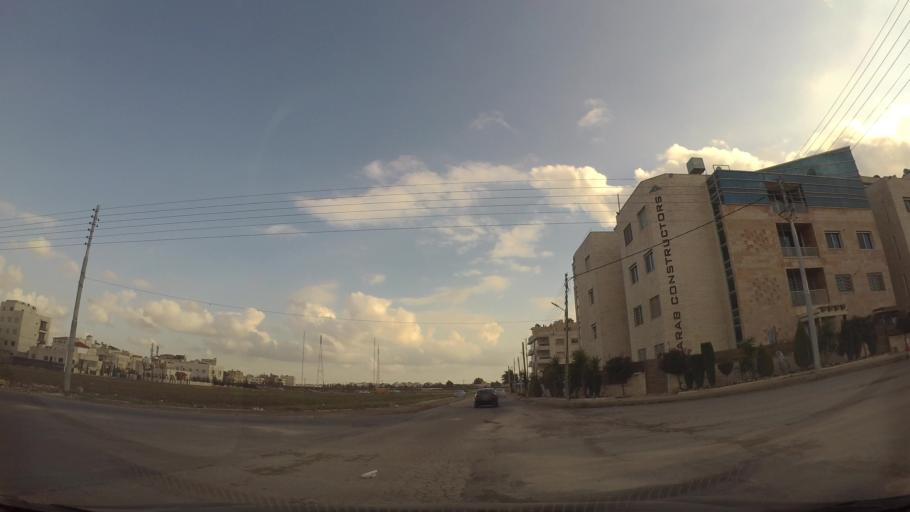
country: JO
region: Amman
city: Al Bunayyat ash Shamaliyah
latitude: 31.9104
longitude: 35.8779
